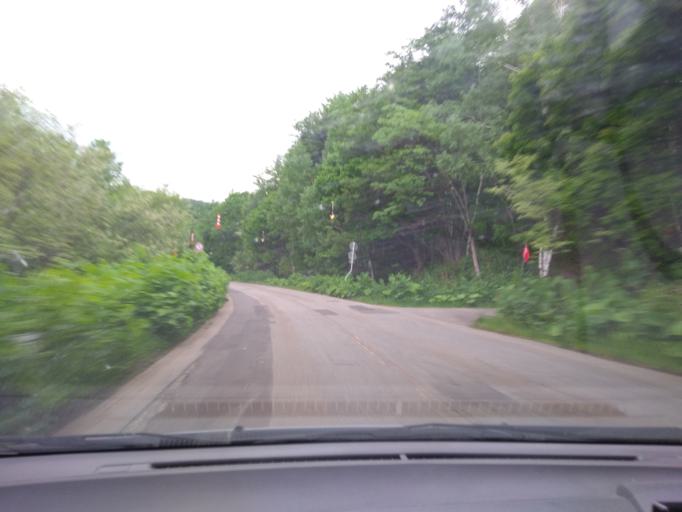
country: JP
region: Hokkaido
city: Shimo-furano
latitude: 43.1382
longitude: 142.4724
